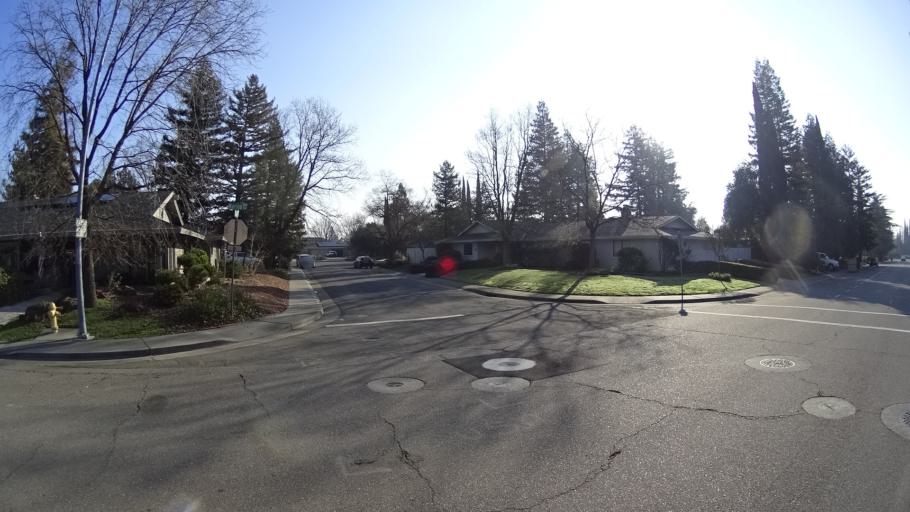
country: US
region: California
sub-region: Yolo County
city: Davis
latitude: 38.5530
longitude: -121.7918
